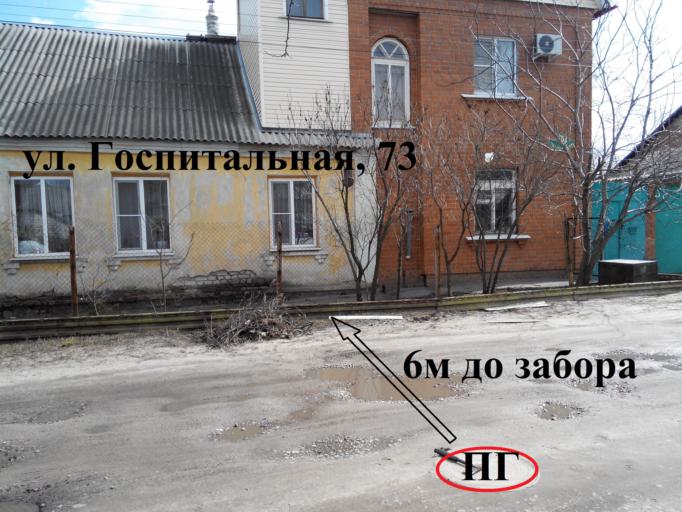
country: RU
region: Voronezj
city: Voronezh
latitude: 51.6361
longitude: 39.1676
